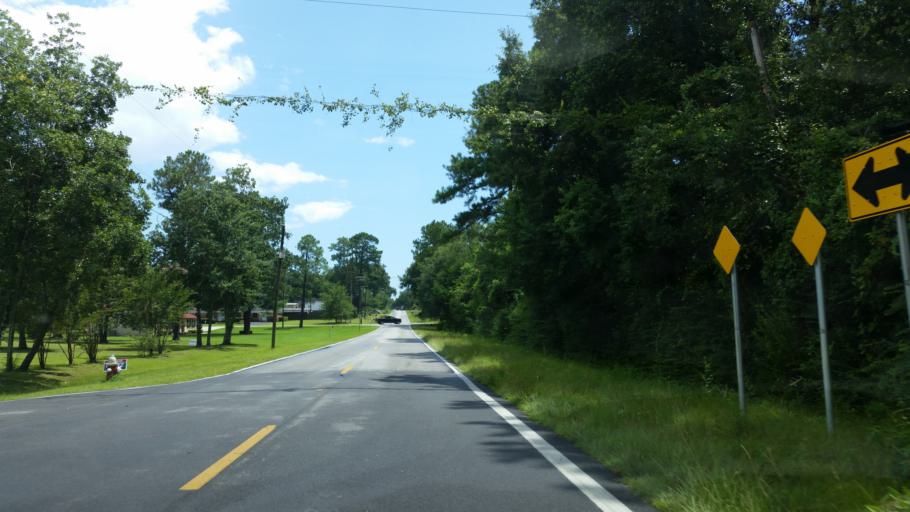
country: US
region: Florida
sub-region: Escambia County
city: Gonzalez
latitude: 30.5501
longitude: -87.3000
